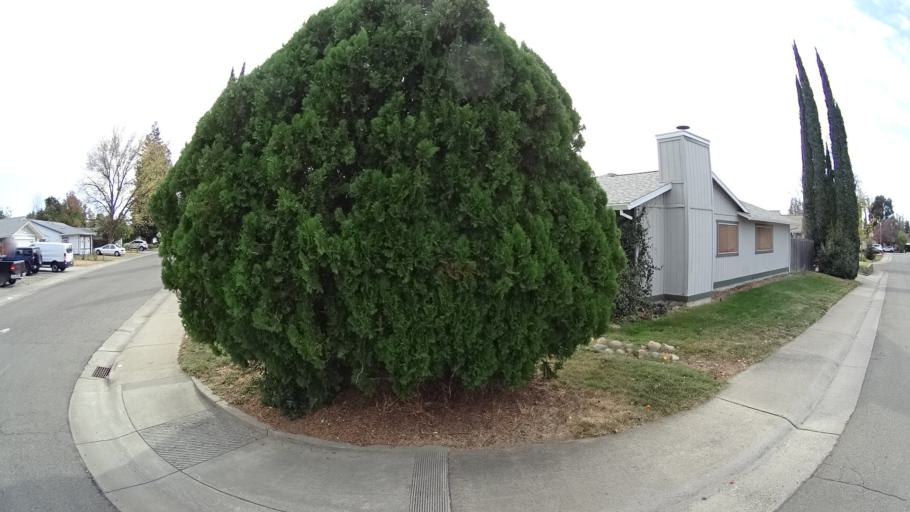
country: US
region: California
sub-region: Sacramento County
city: Citrus Heights
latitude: 38.7097
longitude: -121.2546
